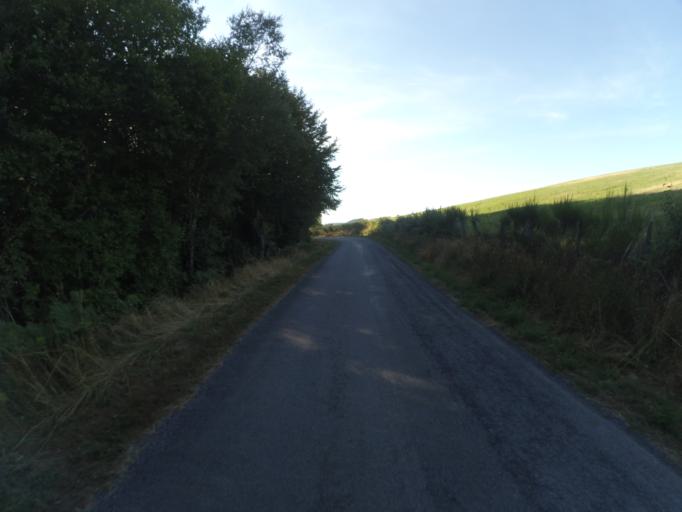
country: FR
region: Limousin
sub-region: Departement de la Creuse
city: Banize
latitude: 45.7402
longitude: 2.0321
